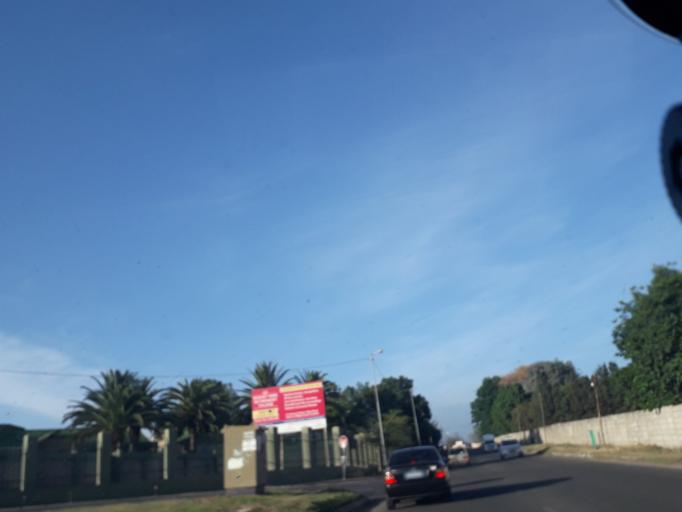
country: ZA
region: Gauteng
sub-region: City of Johannesburg Metropolitan Municipality
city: Roodepoort
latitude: -26.0905
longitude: 27.9022
